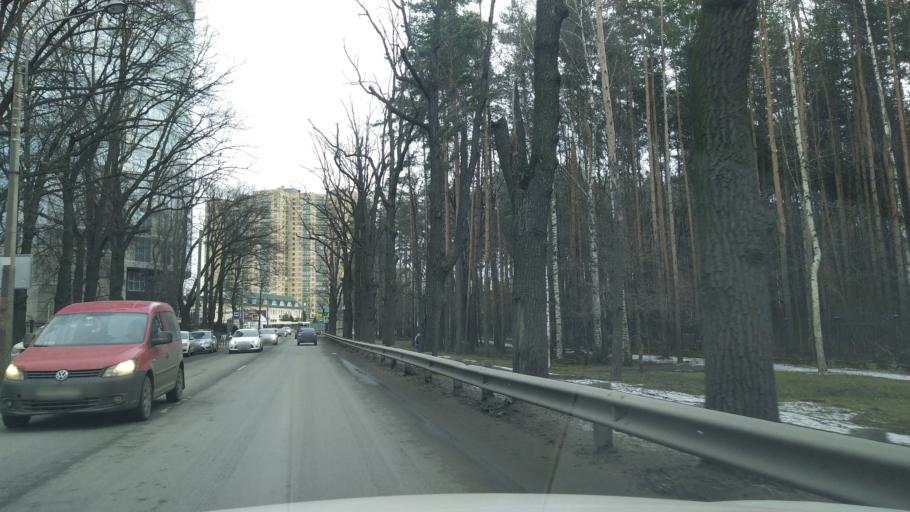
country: RU
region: Leningrad
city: Udel'naya
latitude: 60.0148
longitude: 30.3026
